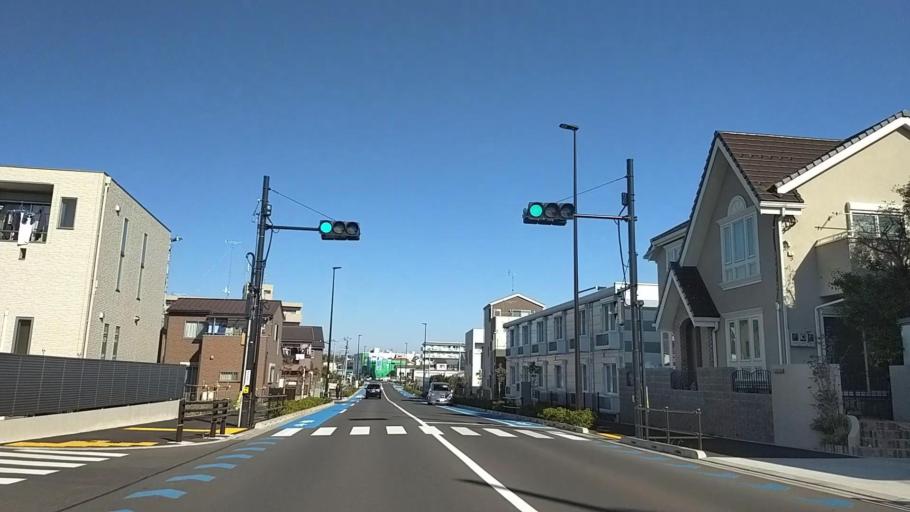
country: JP
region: Tokyo
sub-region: Machida-shi
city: Machida
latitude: 35.5157
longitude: 139.4651
